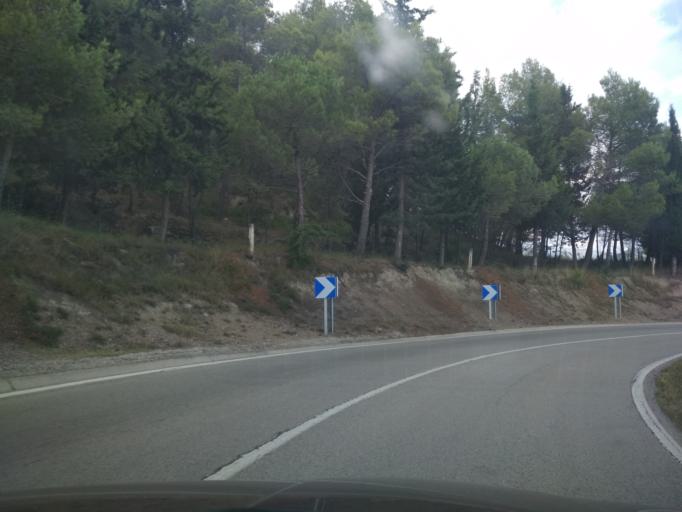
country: ES
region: Catalonia
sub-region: Provincia de Barcelona
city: Sant Feliu de Codines
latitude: 41.6953
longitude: 2.1717
